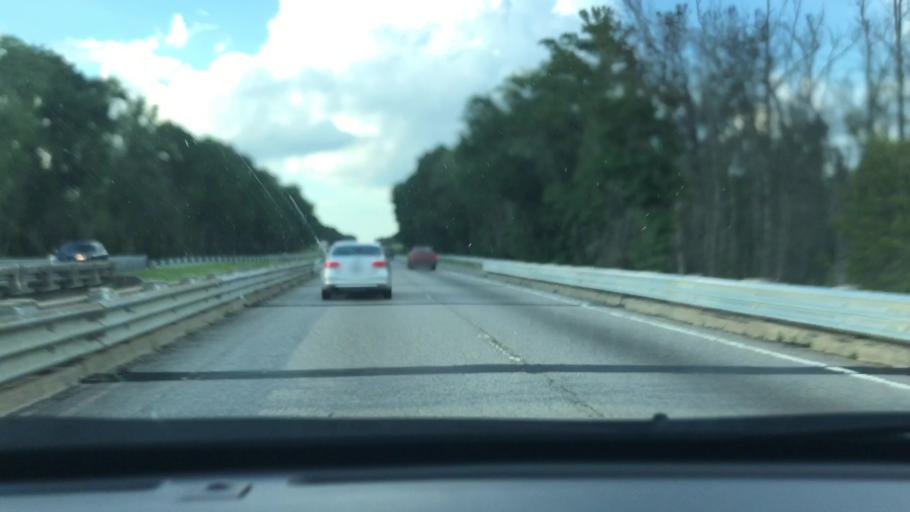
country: US
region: North Carolina
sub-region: Robeson County
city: Saint Pauls
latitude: 34.8586
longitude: -78.9656
